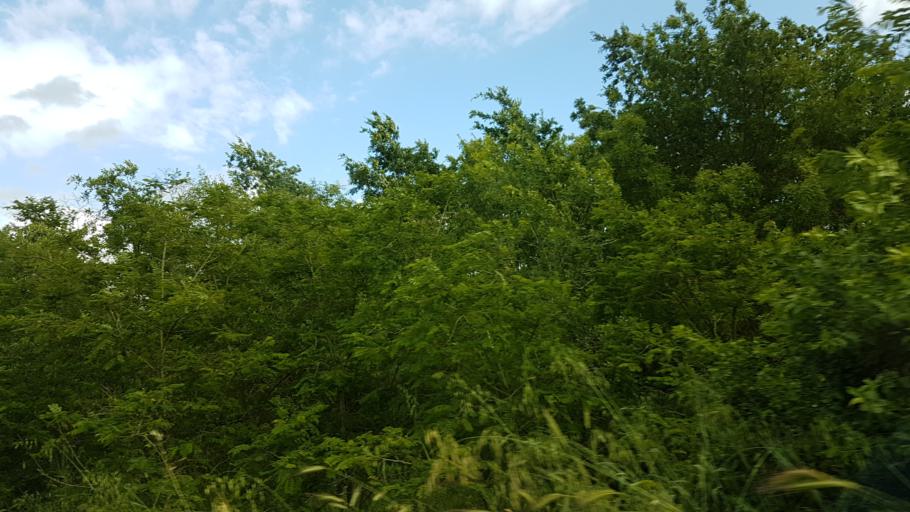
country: IT
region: Tuscany
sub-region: Province of Pisa
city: Santa Luce
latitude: 43.4608
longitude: 10.5346
